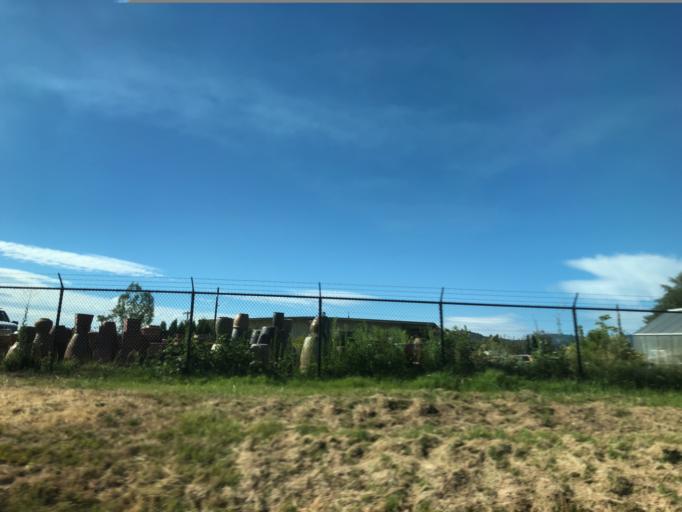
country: US
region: Oregon
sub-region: Josephine County
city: Grants Pass
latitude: 42.4213
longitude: -123.3524
